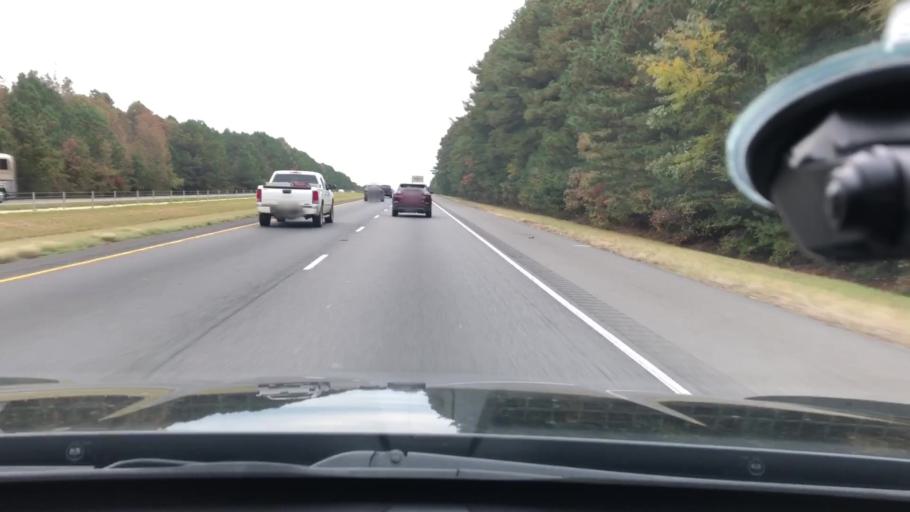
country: US
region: Arkansas
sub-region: Clark County
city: Arkadelphia
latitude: 34.0423
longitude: -93.1393
